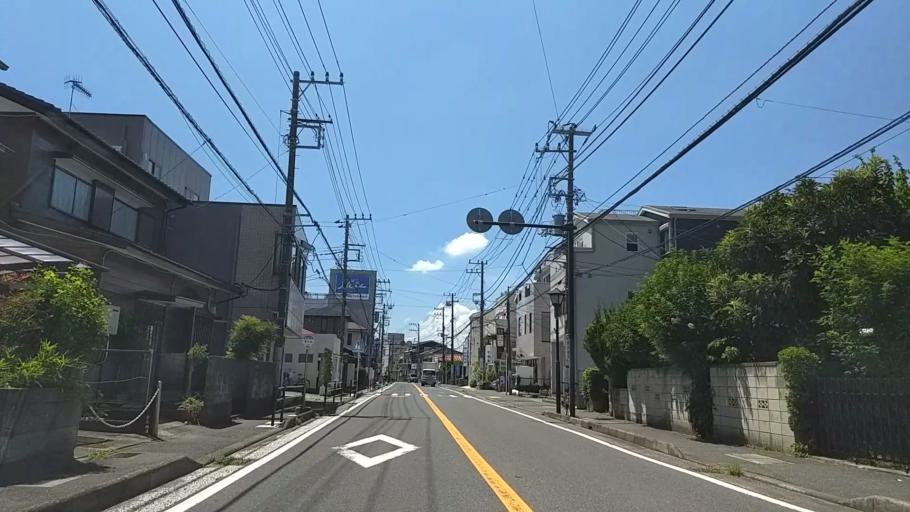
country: JP
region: Kanagawa
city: Zushi
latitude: 35.2974
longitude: 139.5983
